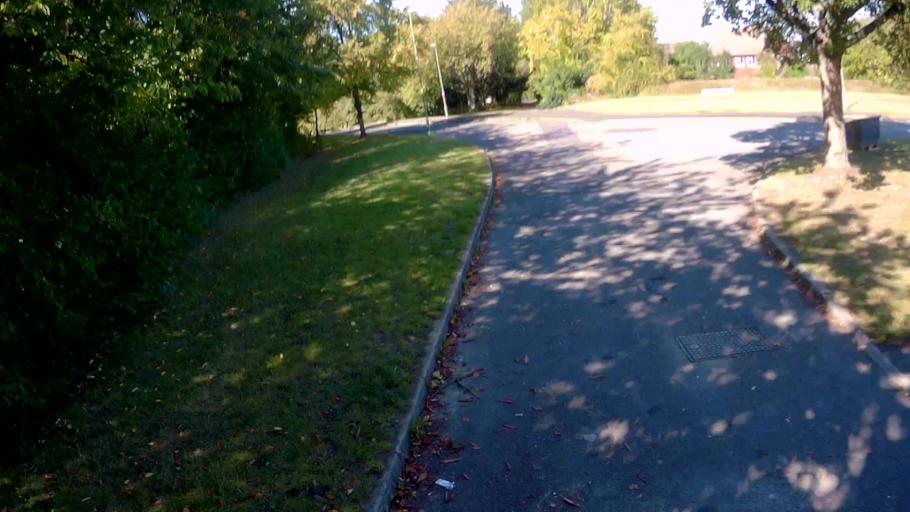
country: GB
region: England
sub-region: Hampshire
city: Basingstoke
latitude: 51.2395
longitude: -1.1272
